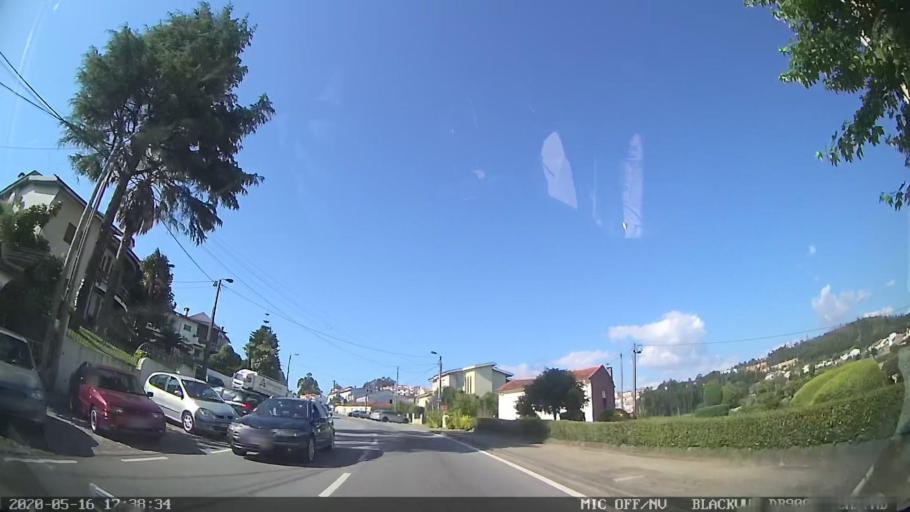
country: PT
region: Porto
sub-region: Gondomar
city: Fanzeres
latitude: 41.1859
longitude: -8.5250
